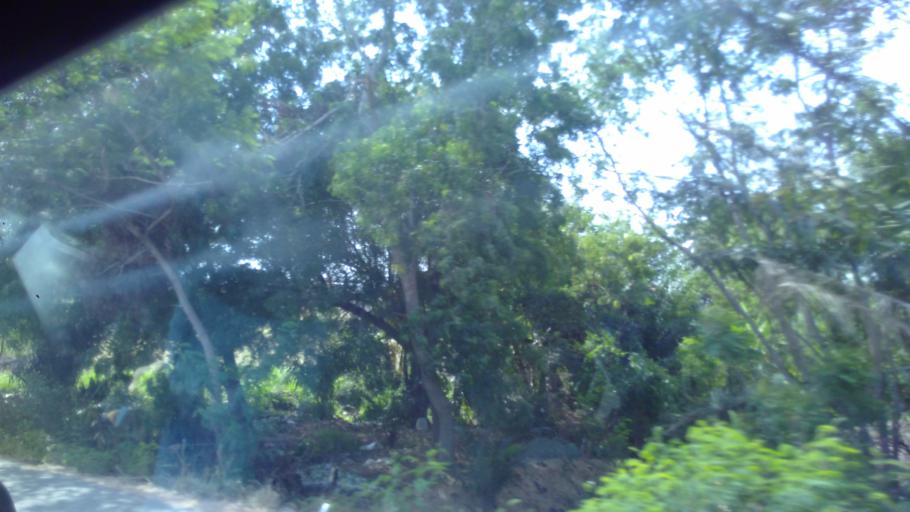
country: GH
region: Greater Accra
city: Nungua
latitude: 5.6156
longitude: -0.0669
